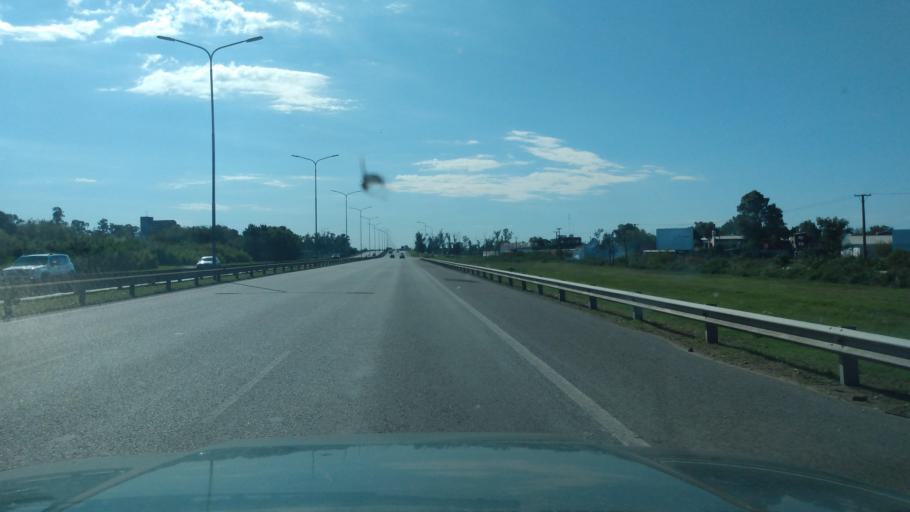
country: AR
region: Buenos Aires
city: Hurlingham
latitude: -34.5379
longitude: -58.5988
